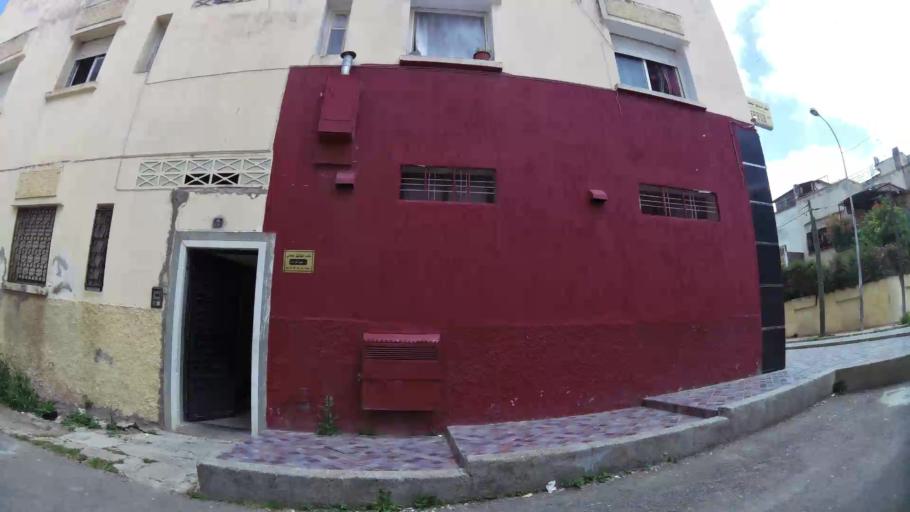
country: MA
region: Fes-Boulemane
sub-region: Fes
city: Fes
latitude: 34.0379
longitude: -5.0207
